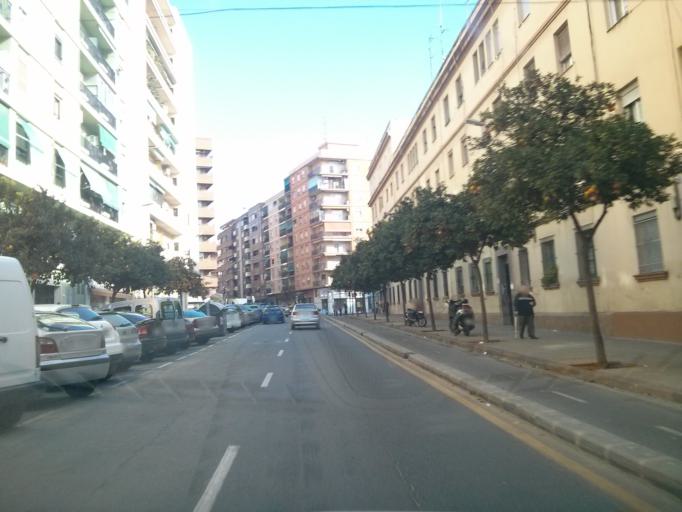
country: ES
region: Valencia
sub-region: Provincia de Valencia
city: Valencia
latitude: 39.4835
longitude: -0.3845
